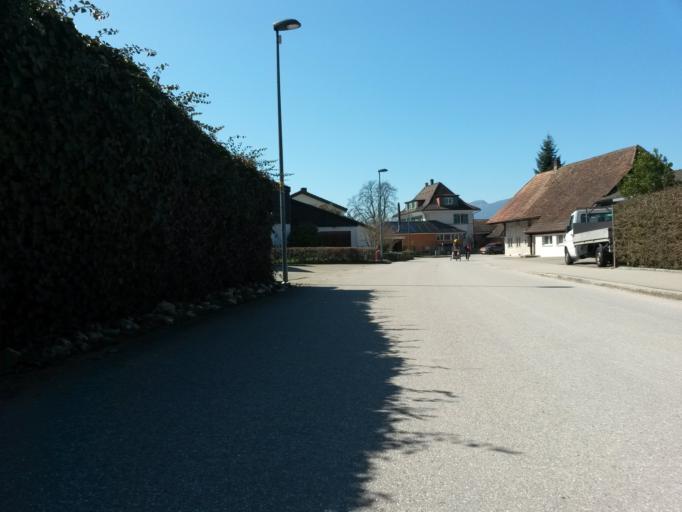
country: CH
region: Solothurn
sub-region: Bezirk Wasseramt
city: Luterbach
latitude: 47.2148
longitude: 7.5929
